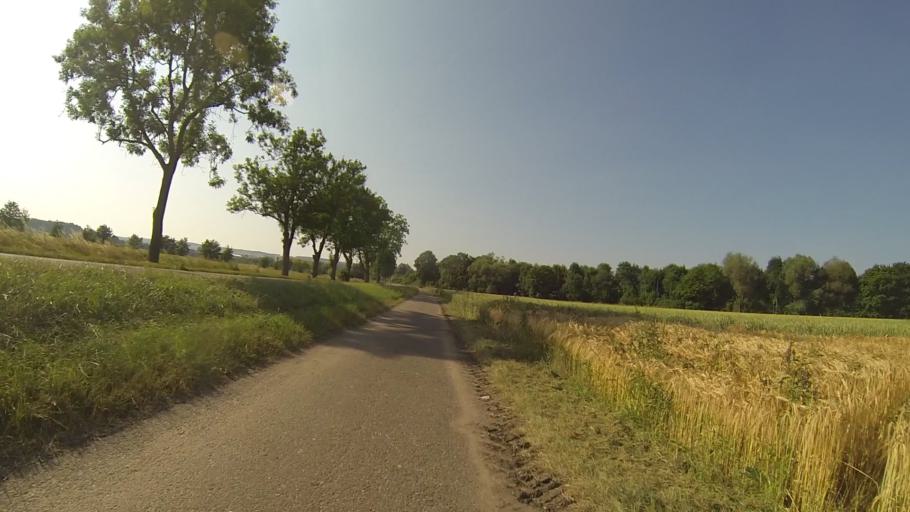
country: DE
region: Baden-Wuerttemberg
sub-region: Tuebingen Region
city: Erbach
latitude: 48.3462
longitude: 9.9357
